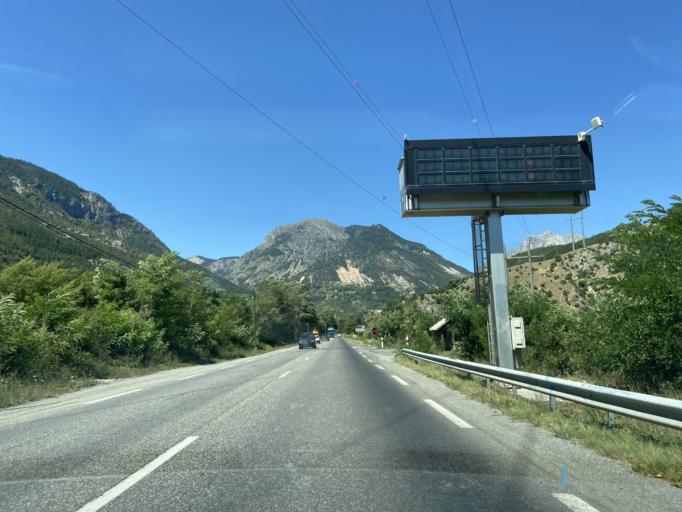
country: FR
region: Provence-Alpes-Cote d'Azur
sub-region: Departement des Hautes-Alpes
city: Saint-Martin-de-Queyrieres
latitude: 44.7652
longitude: 6.5667
